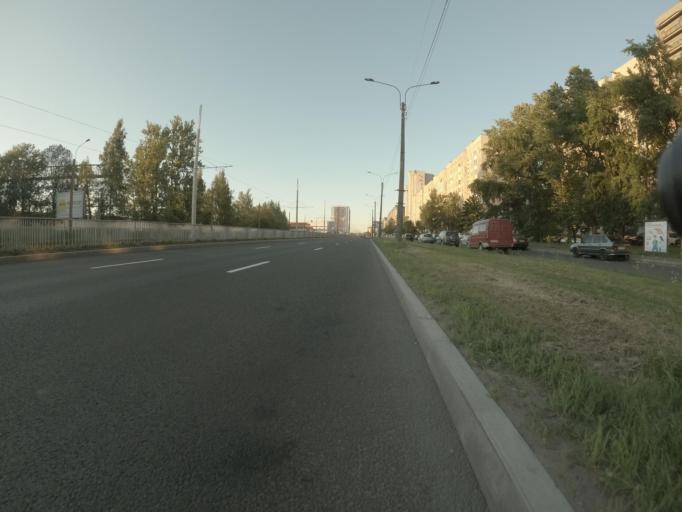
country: RU
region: St.-Petersburg
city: Krasnogvargeisky
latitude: 59.9563
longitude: 30.4695
